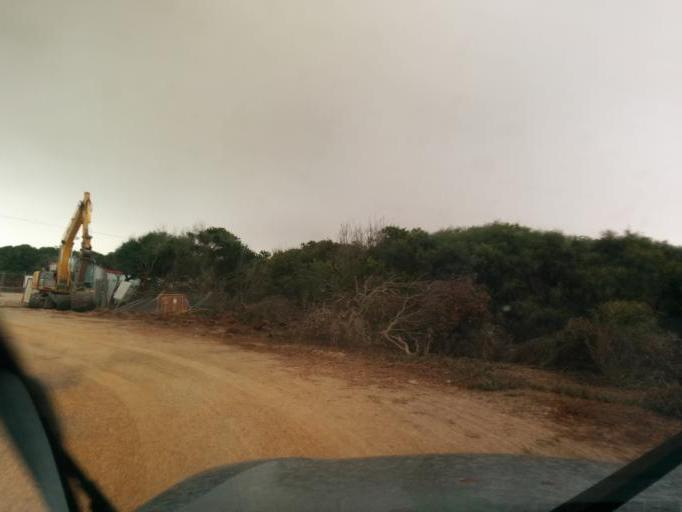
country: PT
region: Beja
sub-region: Odemira
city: Vila Nova de Milfontes
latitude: 37.5981
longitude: -8.8157
